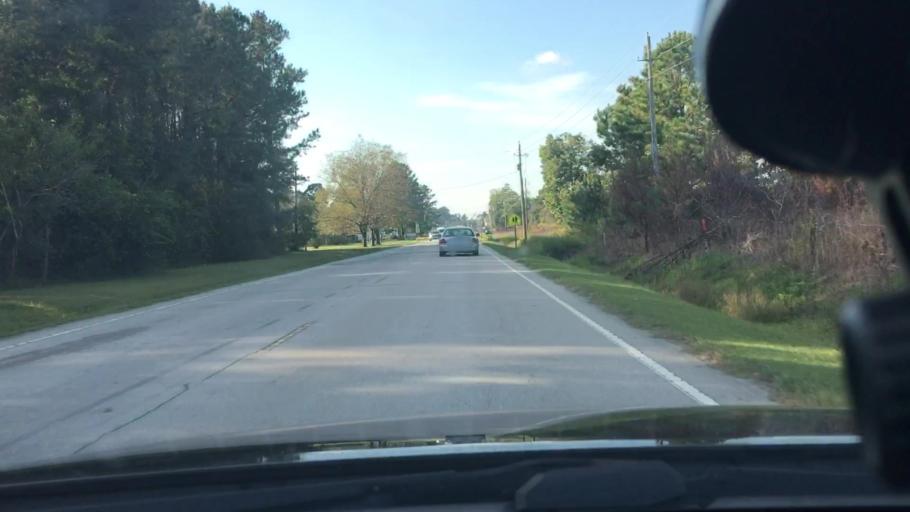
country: US
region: North Carolina
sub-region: Pitt County
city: Windsor
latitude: 35.4602
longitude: -77.2711
